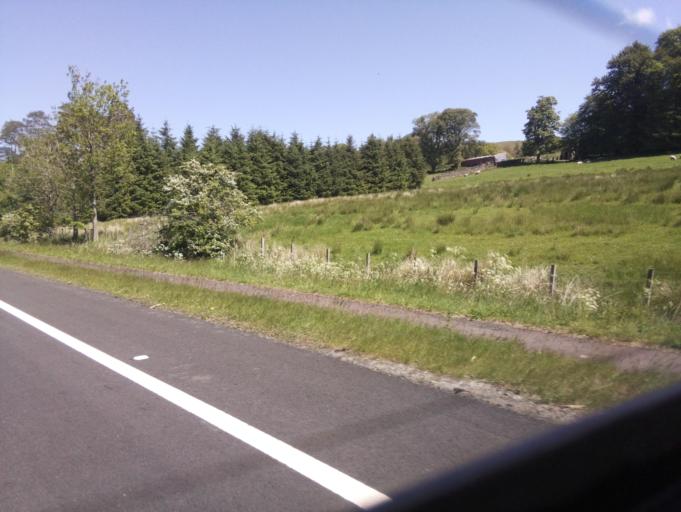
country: GB
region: Scotland
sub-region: The Scottish Borders
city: Hawick
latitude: 55.3317
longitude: -2.9417
